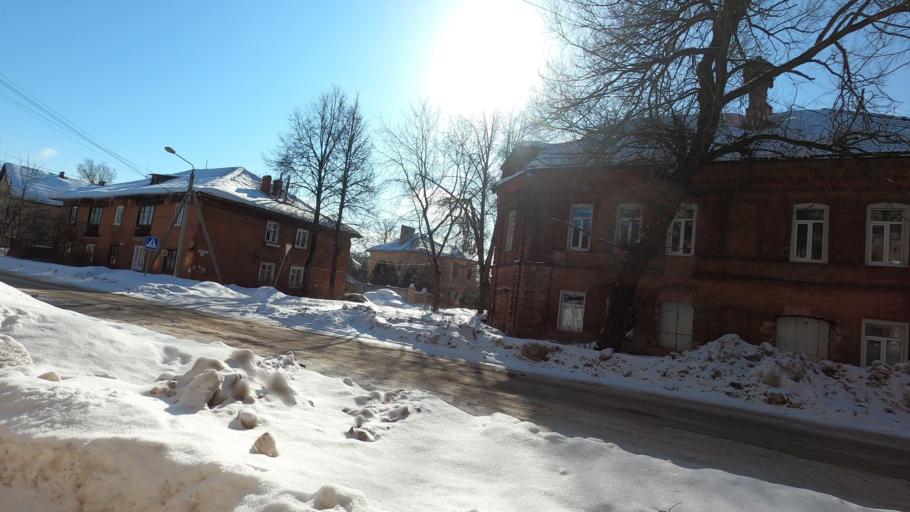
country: RU
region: Jaroslavl
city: Rybinsk
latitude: 58.0464
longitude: 38.8641
